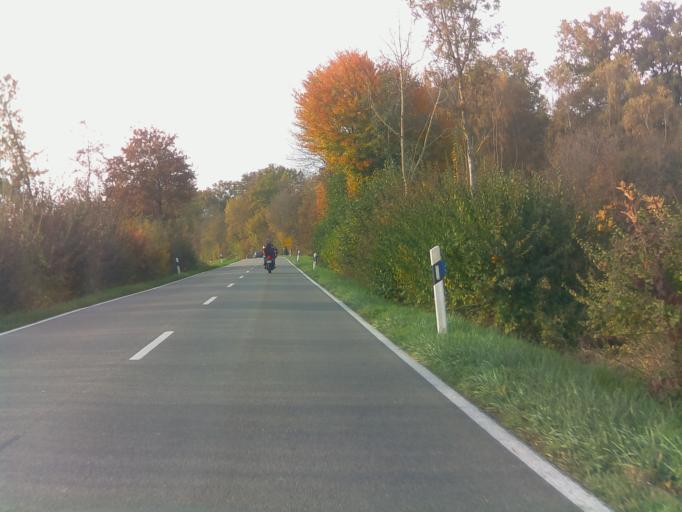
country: DE
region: Baden-Wuerttemberg
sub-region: Karlsruhe Region
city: Aglasterhausen
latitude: 49.3607
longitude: 8.9758
